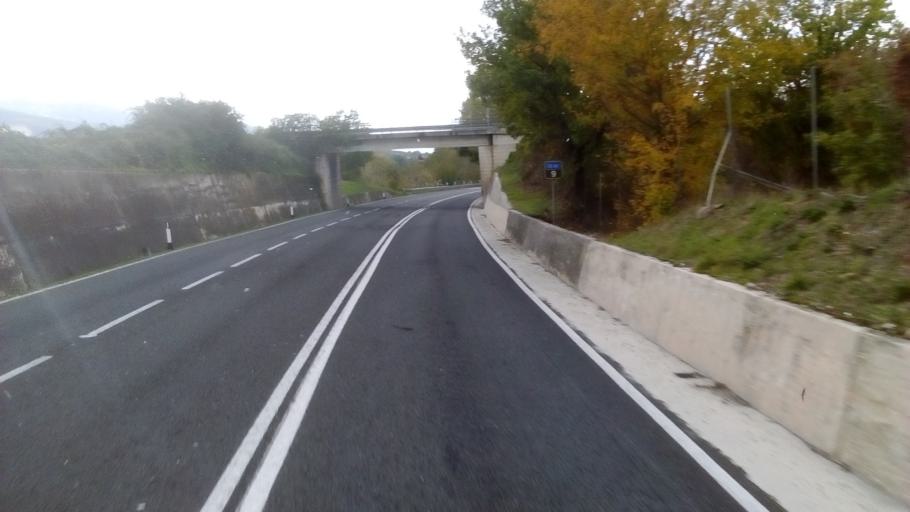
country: IT
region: Molise
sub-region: Provincia di Isernia
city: Isernia
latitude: 41.5820
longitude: 14.2310
